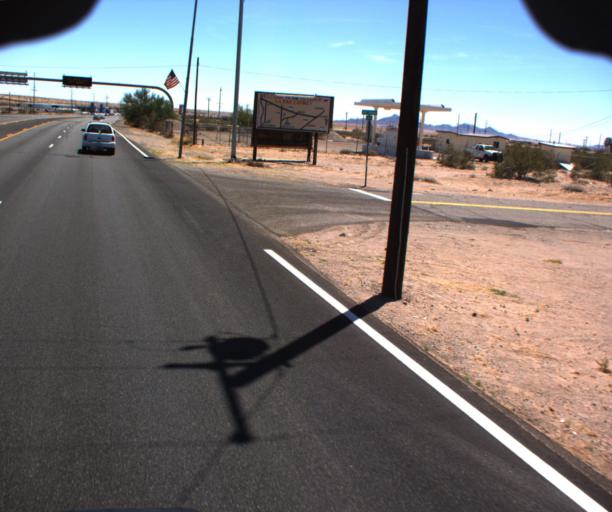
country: US
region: Arizona
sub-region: La Paz County
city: Parker
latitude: 34.1397
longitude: -114.2826
